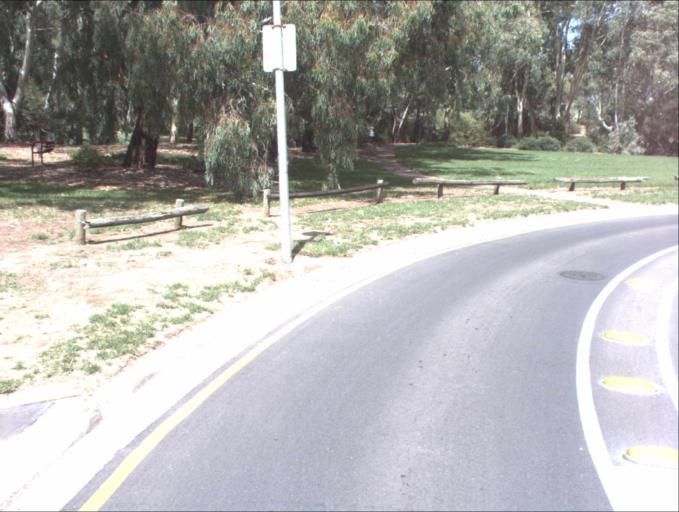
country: AU
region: South Australia
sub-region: Campbelltown
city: Paradise
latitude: -34.8670
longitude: 138.6680
